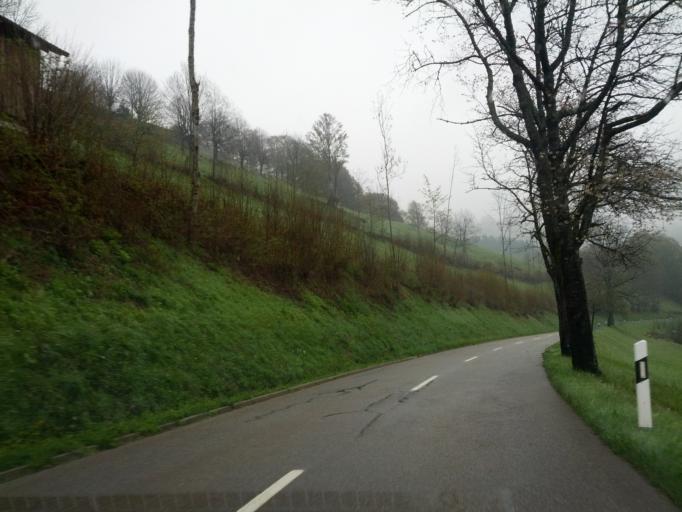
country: DE
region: Baden-Wuerttemberg
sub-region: Freiburg Region
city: Wieden
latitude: 47.8420
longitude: 7.8835
